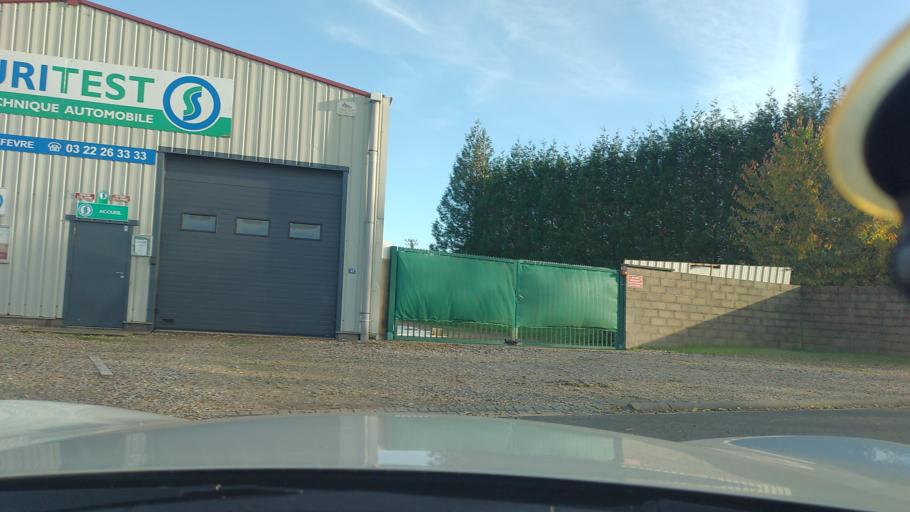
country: FR
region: Picardie
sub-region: Departement de la Somme
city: Fressenneville
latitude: 50.0628
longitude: 1.5784
